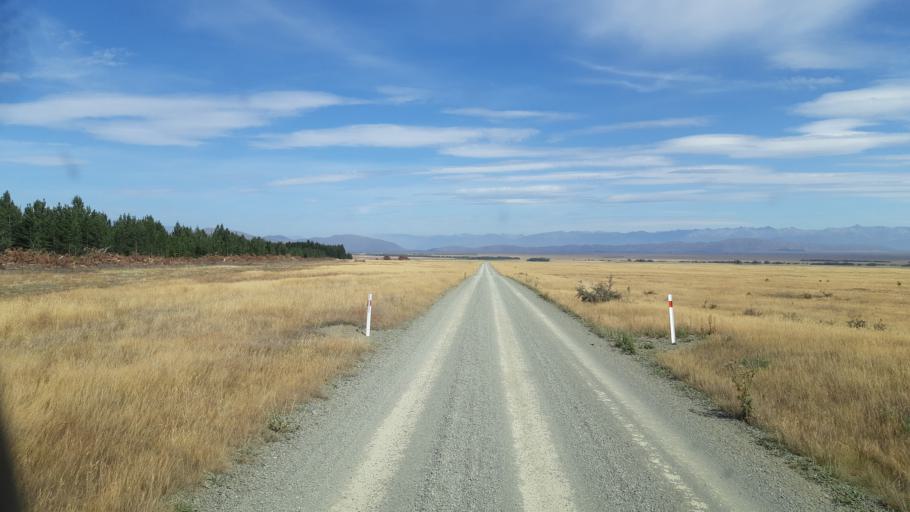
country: NZ
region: Canterbury
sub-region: Timaru District
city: Pleasant Point
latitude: -44.1940
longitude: 170.5624
